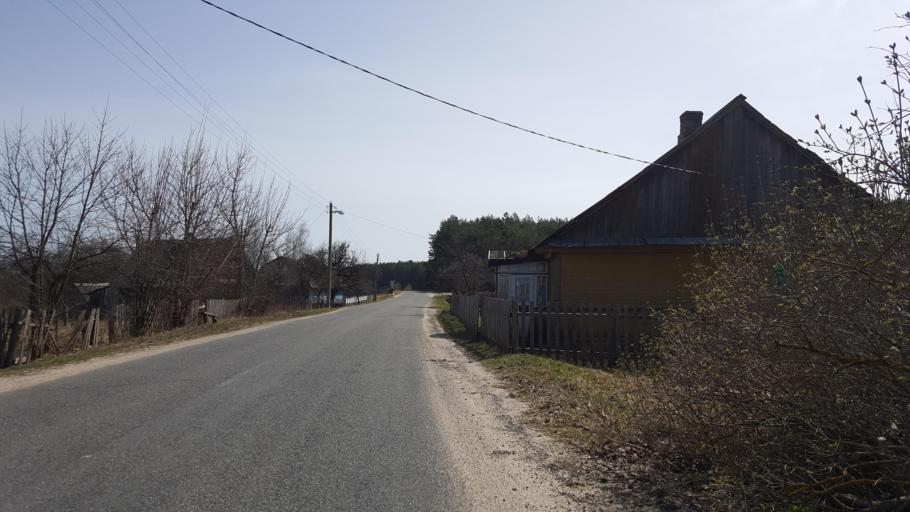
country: BY
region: Brest
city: Kamyanyuki
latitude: 52.5190
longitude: 23.8502
